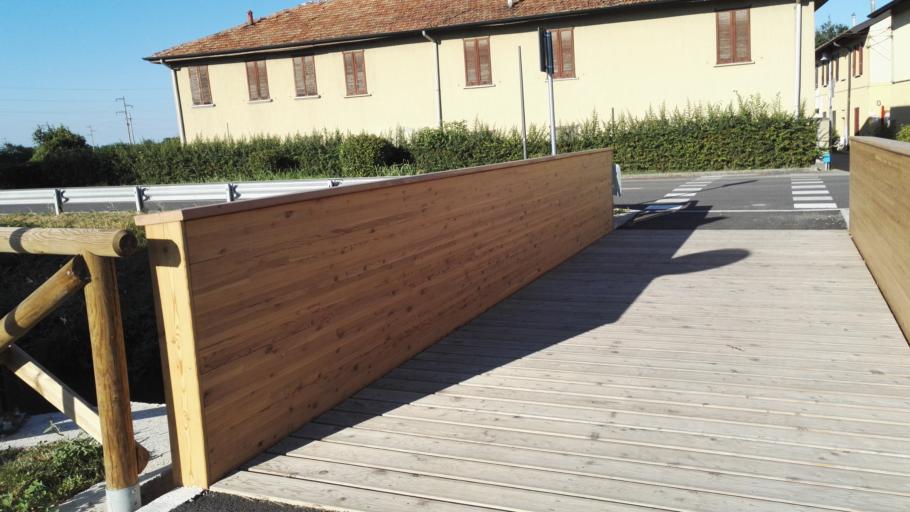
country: IT
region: Lombardy
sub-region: Citta metropolitana di Milano
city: Locate di Triulzi
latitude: 45.3619
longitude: 9.2191
